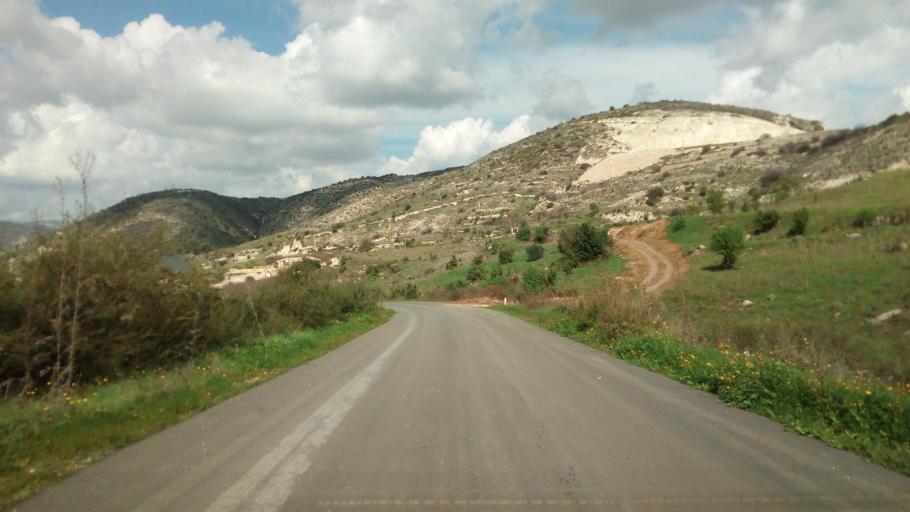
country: CY
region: Pafos
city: Mesogi
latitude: 34.7836
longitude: 32.5472
